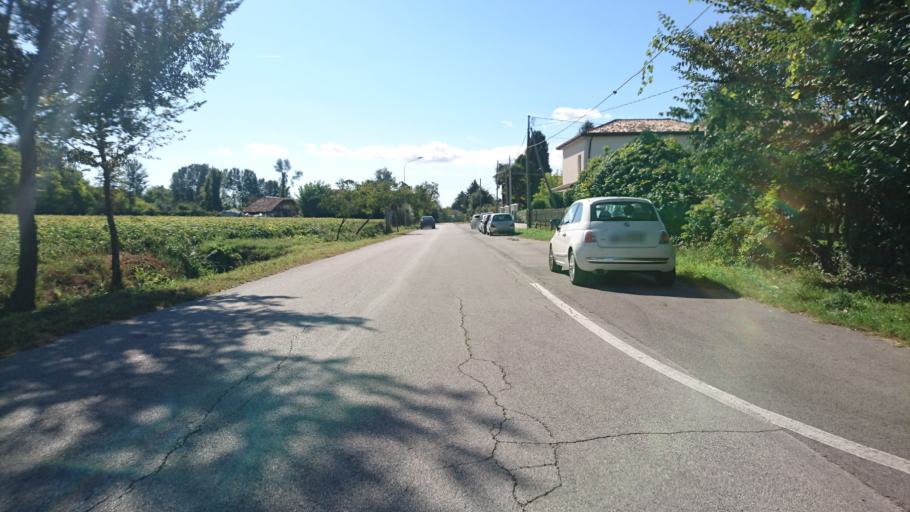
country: IT
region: Veneto
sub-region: Provincia di Venezia
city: Vigonovo
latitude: 45.3959
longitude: 12.0032
